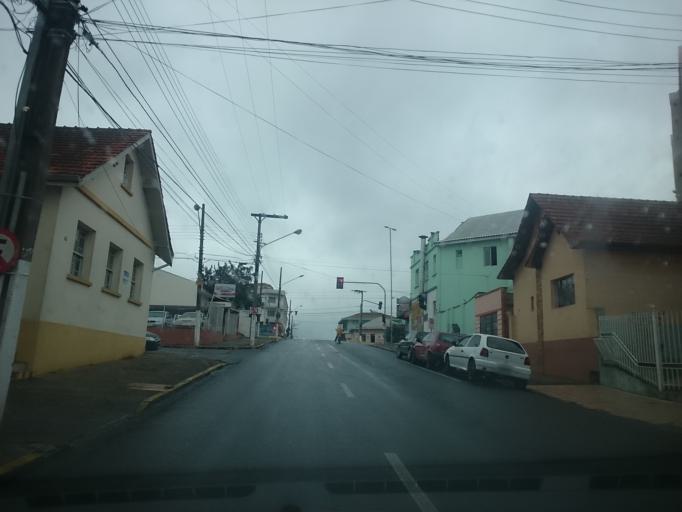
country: BR
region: Santa Catarina
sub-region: Lages
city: Lages
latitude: -27.8186
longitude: -50.3314
